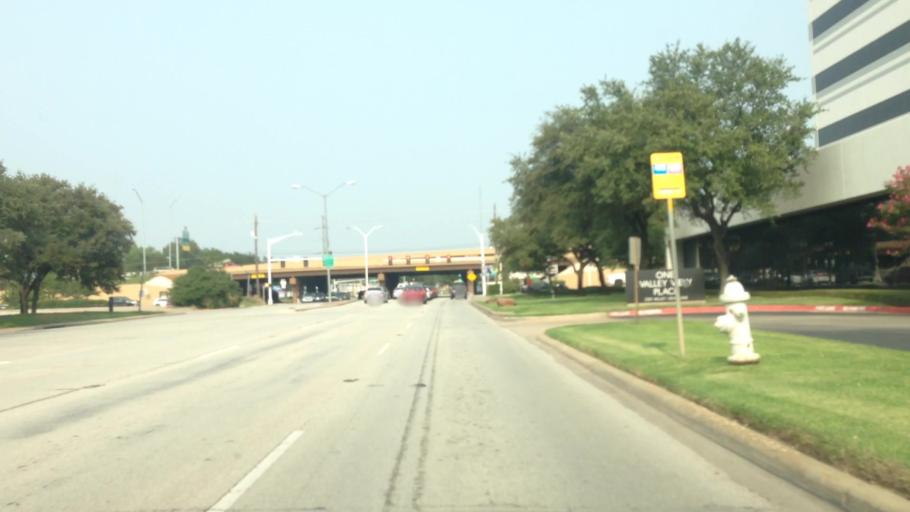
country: US
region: Texas
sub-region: Dallas County
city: Farmers Branch
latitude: 32.9222
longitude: -96.9018
